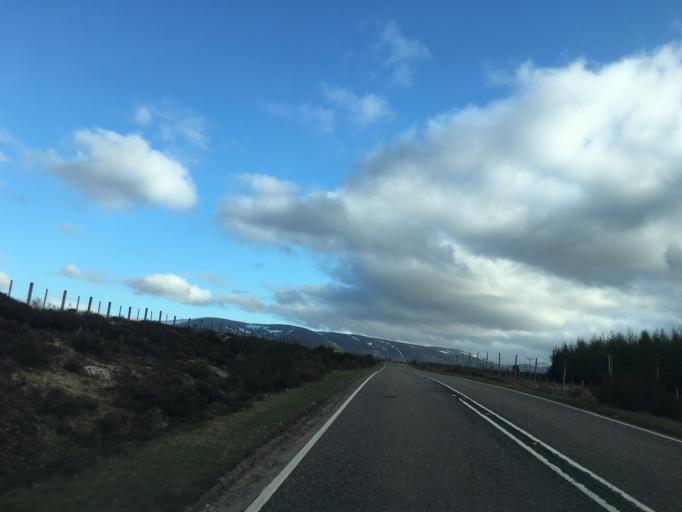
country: GB
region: Scotland
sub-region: Highland
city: Kingussie
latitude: 56.9765
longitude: -4.2357
